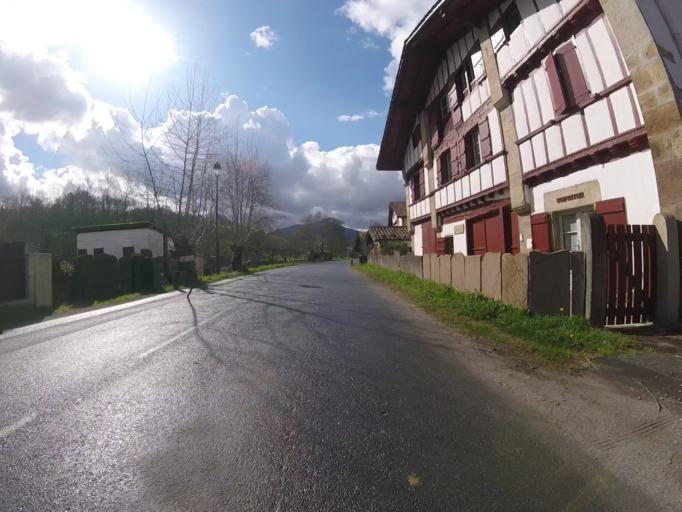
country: FR
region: Aquitaine
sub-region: Departement des Pyrenees-Atlantiques
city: Sare
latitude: 43.3063
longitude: -1.5724
